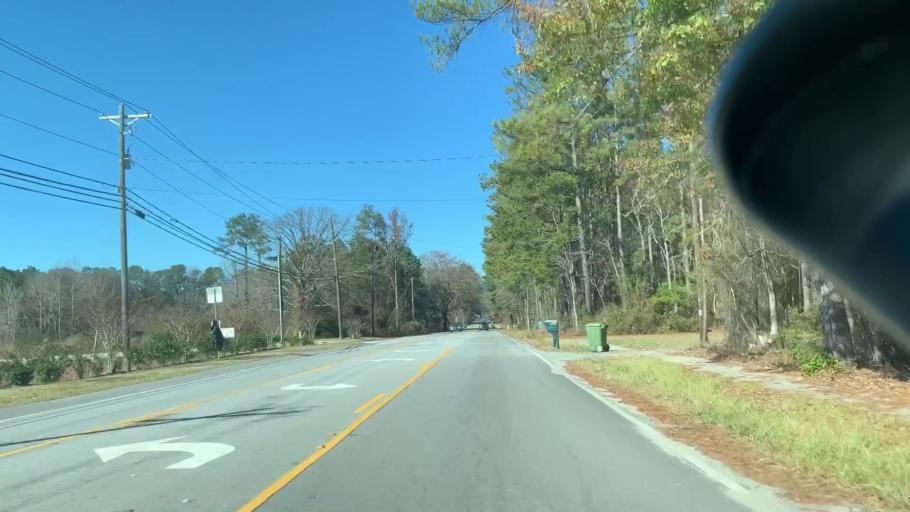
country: US
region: South Carolina
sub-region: Richland County
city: Woodfield
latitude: 34.0769
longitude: -80.9195
